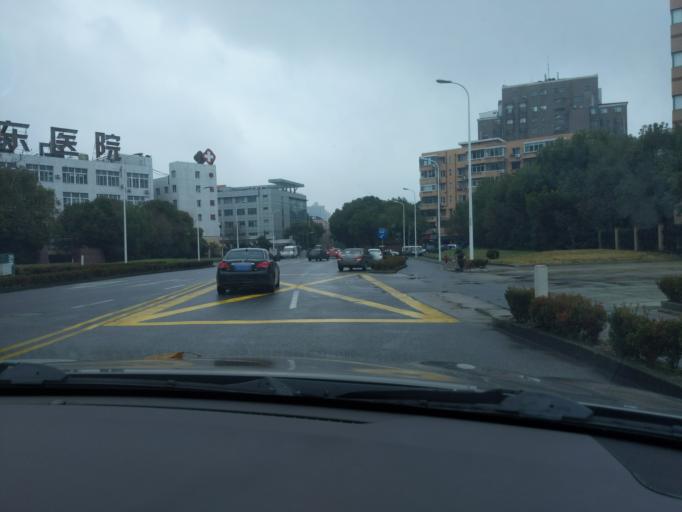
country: CN
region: Shanghai Shi
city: Huamu
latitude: 31.1875
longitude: 121.5257
